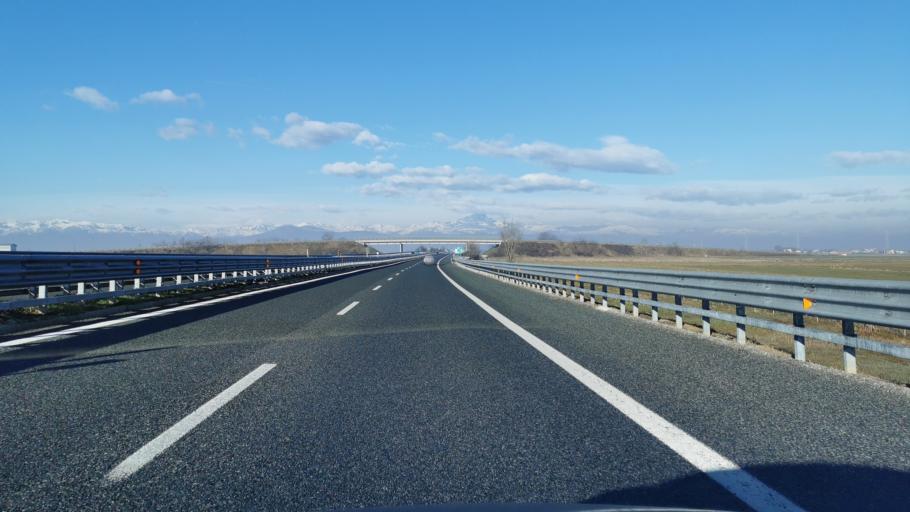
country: IT
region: Piedmont
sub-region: Provincia di Cuneo
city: Sant'Albano Stura
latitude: 44.4701
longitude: 7.7138
